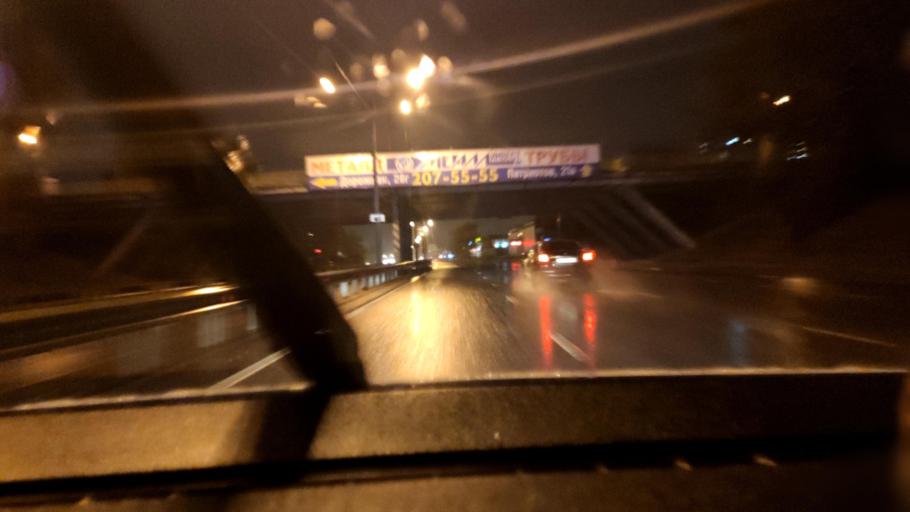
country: RU
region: Voronezj
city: Voronezh
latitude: 51.6617
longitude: 39.1304
